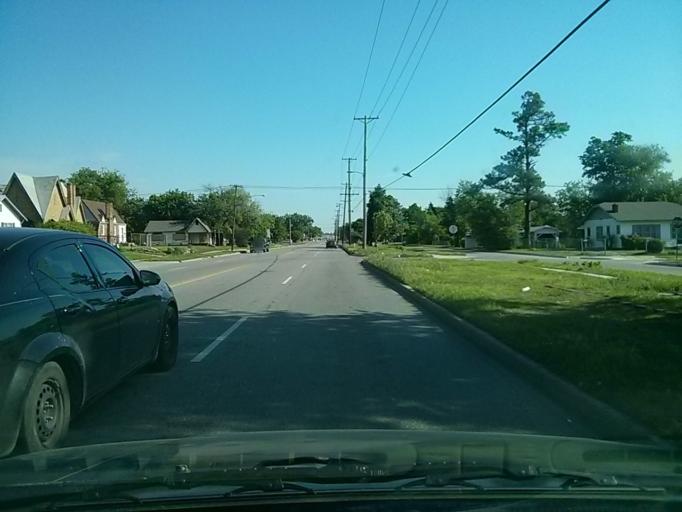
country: US
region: Oklahoma
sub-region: Tulsa County
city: Tulsa
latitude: 36.1865
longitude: -95.9934
